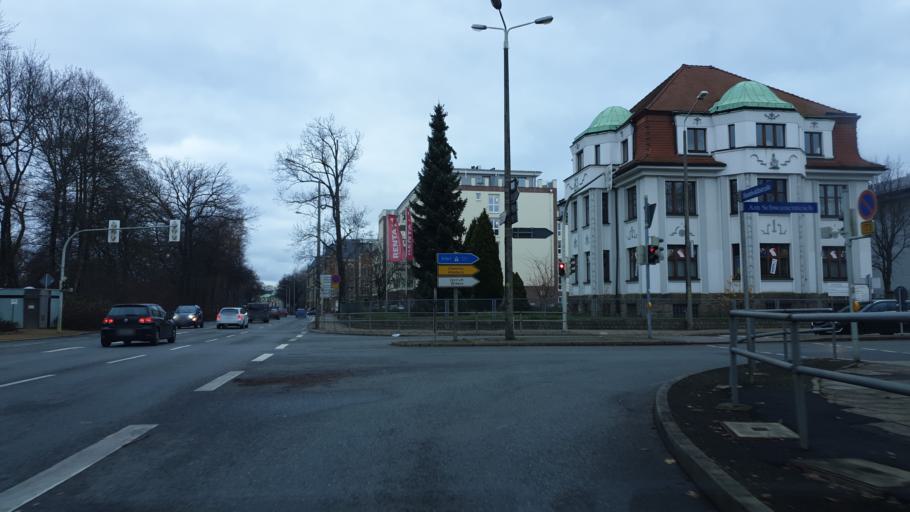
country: DE
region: Saxony
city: Zwickau
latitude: 50.7141
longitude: 12.4939
